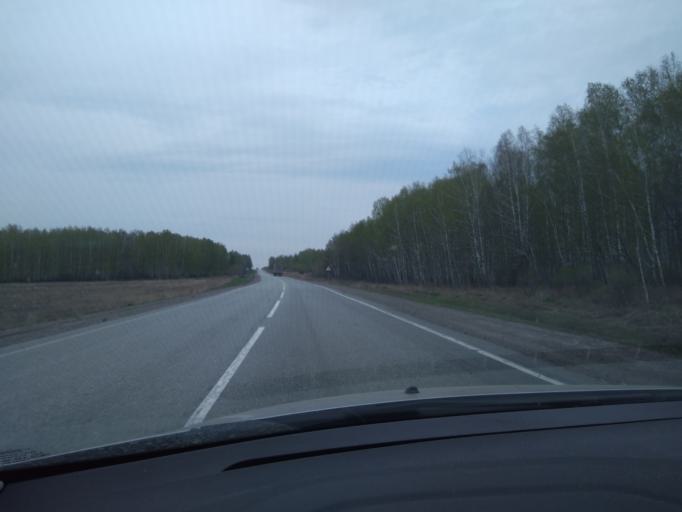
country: RU
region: Sverdlovsk
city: Yelanskiy
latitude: 56.7606
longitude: 62.4001
